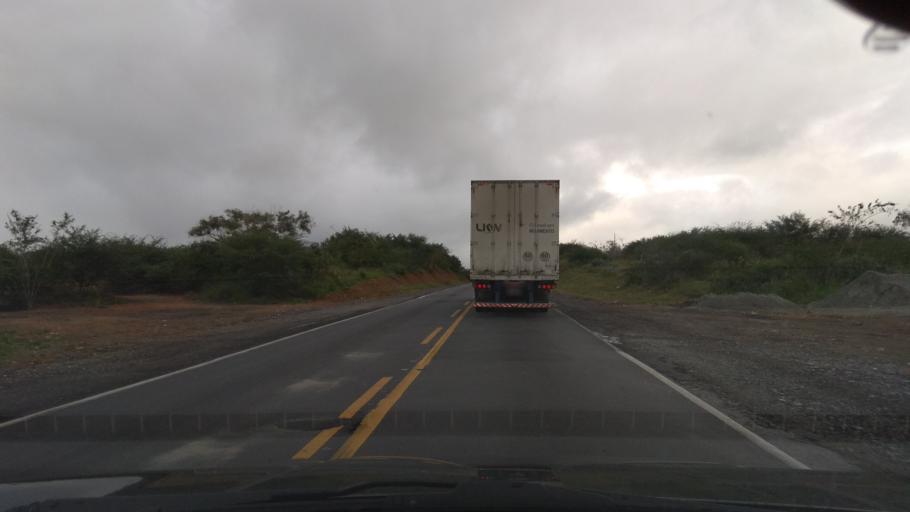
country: BR
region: Bahia
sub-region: Jaguaquara
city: Jaguaquara
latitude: -13.3796
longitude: -40.0205
